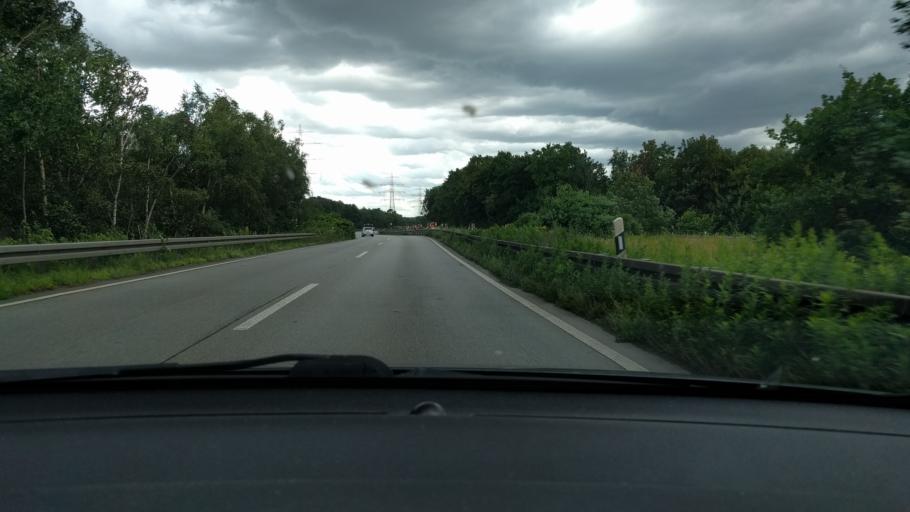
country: DE
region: North Rhine-Westphalia
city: Waltrop
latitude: 51.5850
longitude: 7.3667
